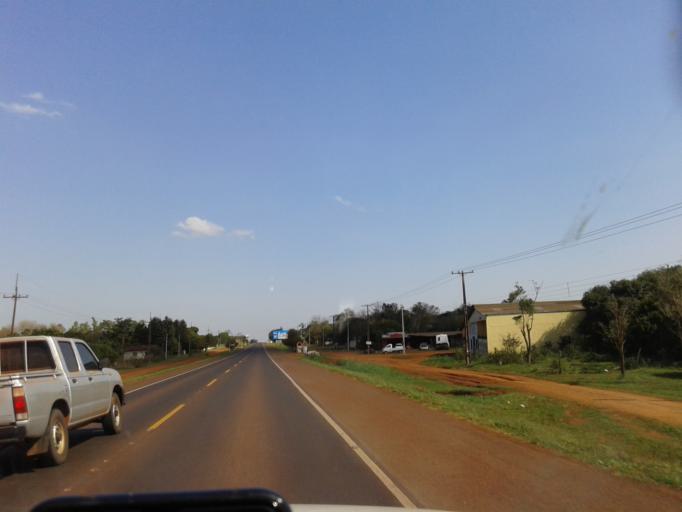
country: PY
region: Alto Parana
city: Santa Rita
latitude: -25.6684
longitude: -54.9971
